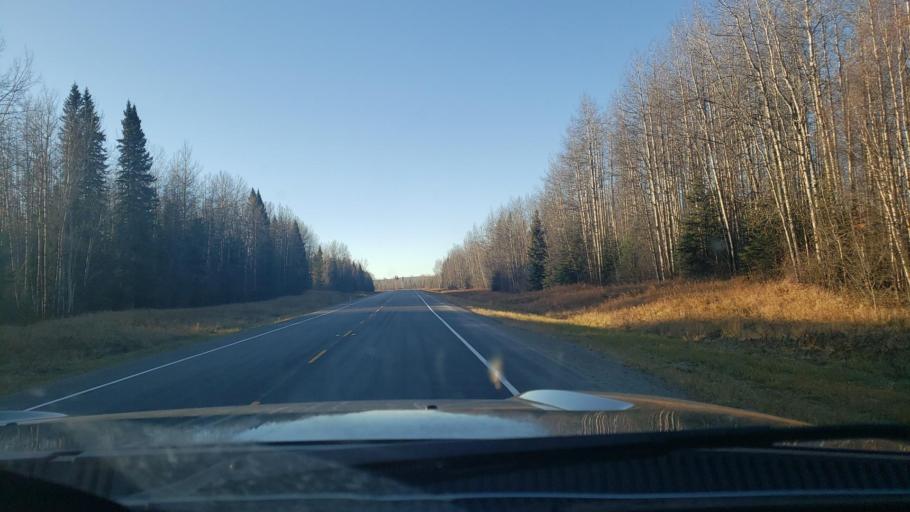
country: CA
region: British Columbia
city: Fort Nelson
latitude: 57.9940
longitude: -122.7493
